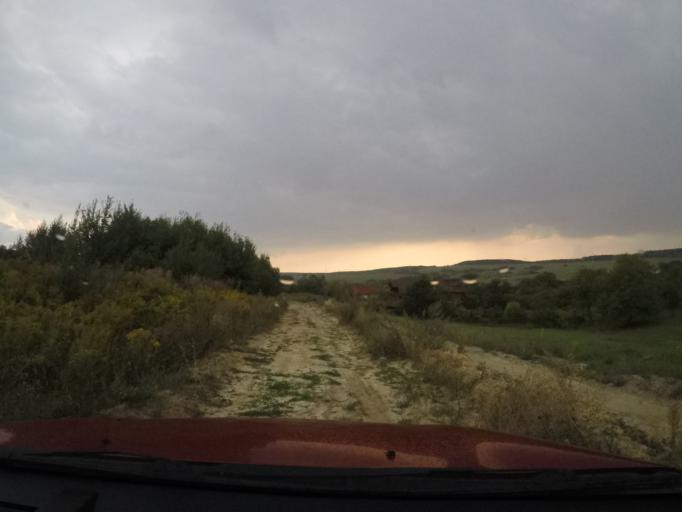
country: SK
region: Kosicky
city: Kosice
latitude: 48.6897
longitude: 21.1978
